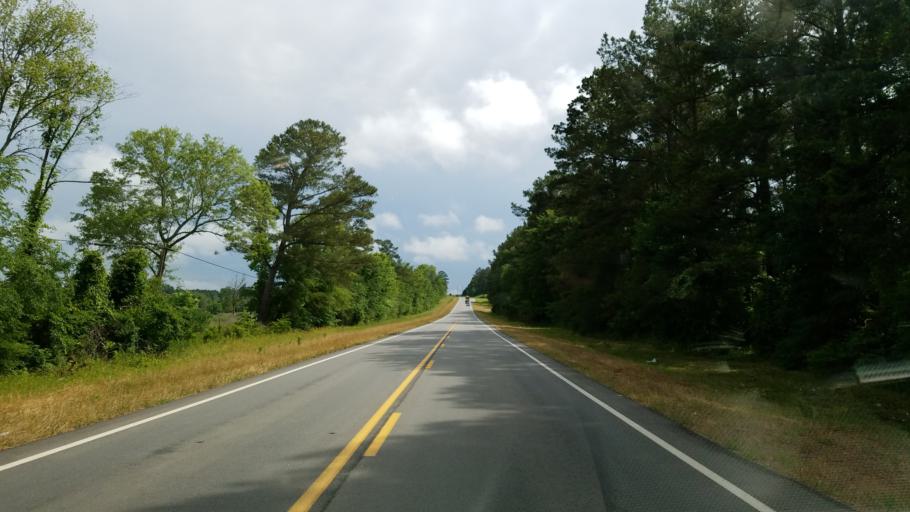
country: US
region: Georgia
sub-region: Houston County
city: Perry
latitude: 32.3973
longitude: -83.7851
